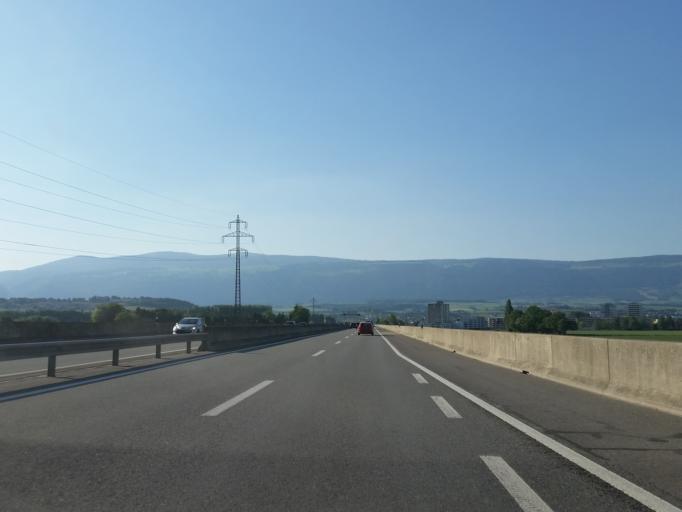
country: CH
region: Vaud
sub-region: Jura-Nord vaudois District
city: Yverdon-les-Bains
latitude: 46.7625
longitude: 6.6340
